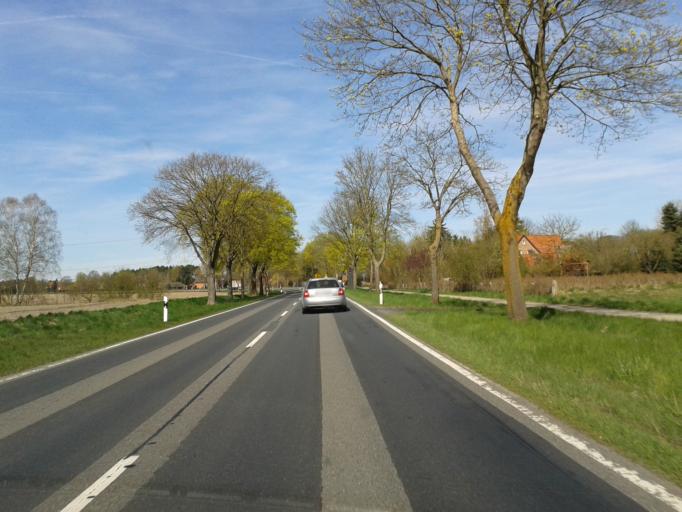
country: DE
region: Lower Saxony
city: Gerdau
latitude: 52.9671
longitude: 10.3971
